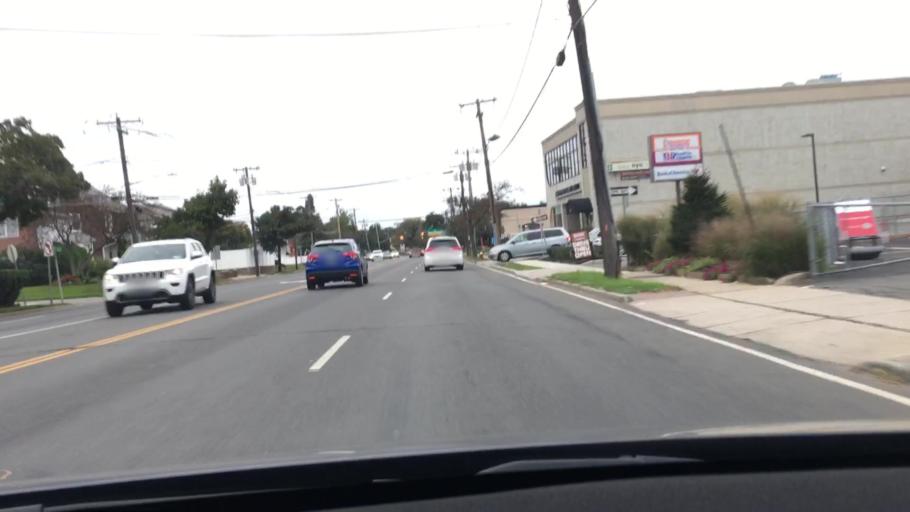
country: US
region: New York
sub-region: Nassau County
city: Carle Place
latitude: 40.7501
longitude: -73.6181
